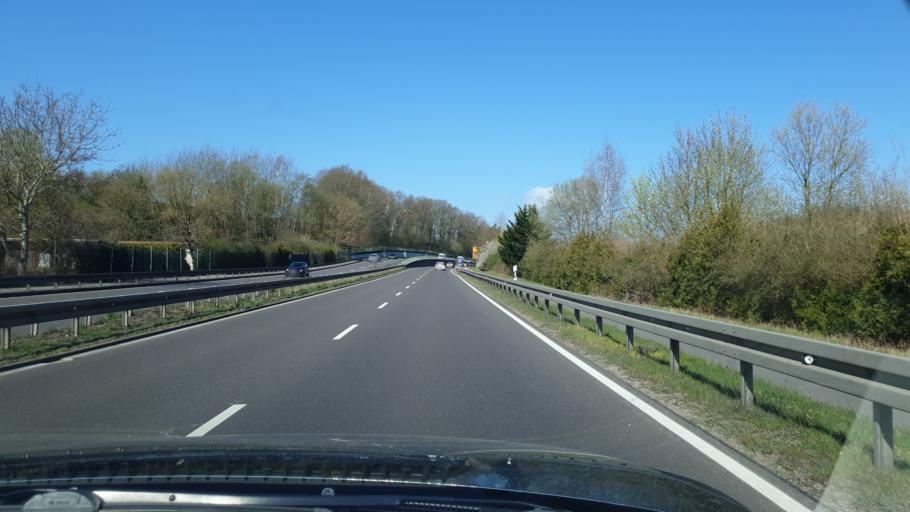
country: DE
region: Mecklenburg-Vorpommern
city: Neumuehle
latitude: 53.6209
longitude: 11.3677
